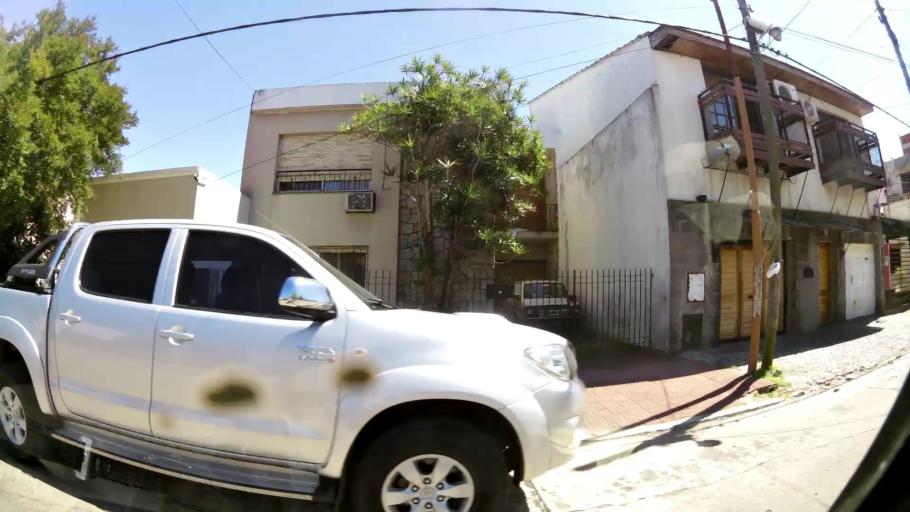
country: AR
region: Buenos Aires
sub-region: Partido de Quilmes
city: Quilmes
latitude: -34.7265
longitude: -58.2715
